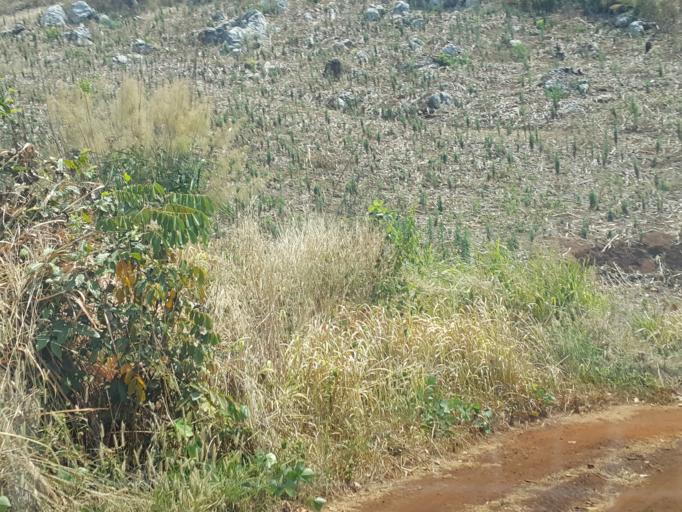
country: TH
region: Chiang Mai
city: Samoeng
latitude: 18.7754
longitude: 98.8272
